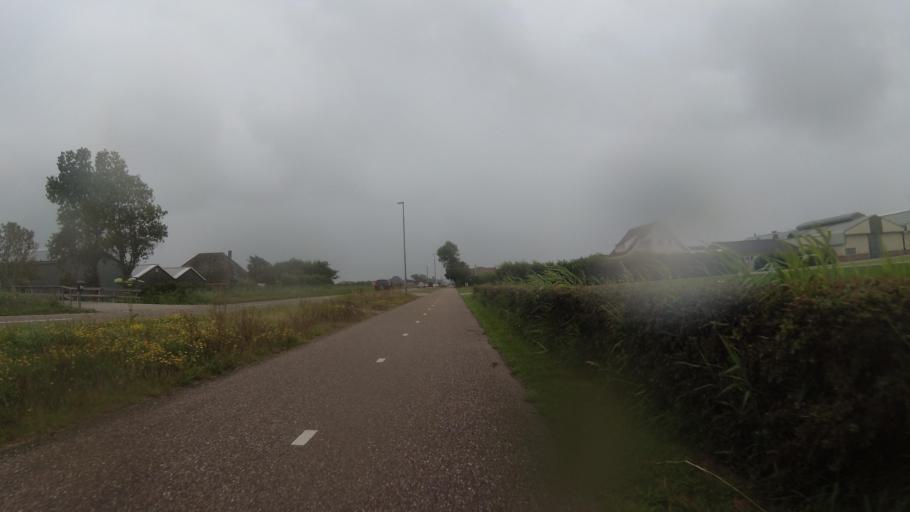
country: NL
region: North Holland
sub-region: Gemeente Den Helder
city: Den Helder
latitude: 52.9065
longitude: 4.7528
